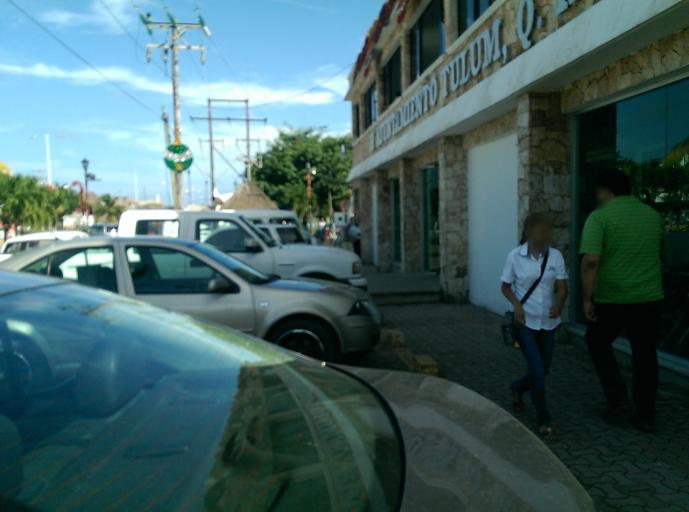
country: MX
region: Quintana Roo
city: Tulum
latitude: 20.2106
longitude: -87.4636
